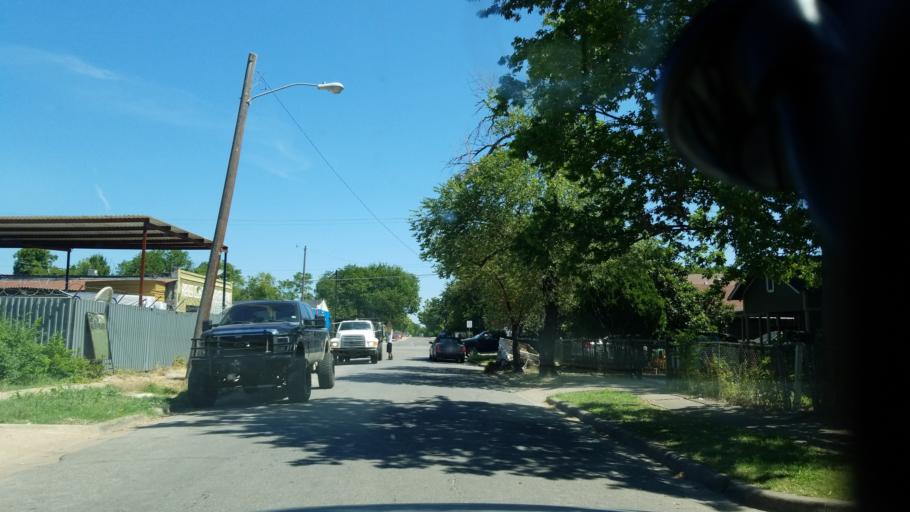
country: US
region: Texas
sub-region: Dallas County
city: Cockrell Hill
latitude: 32.7125
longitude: -96.8194
